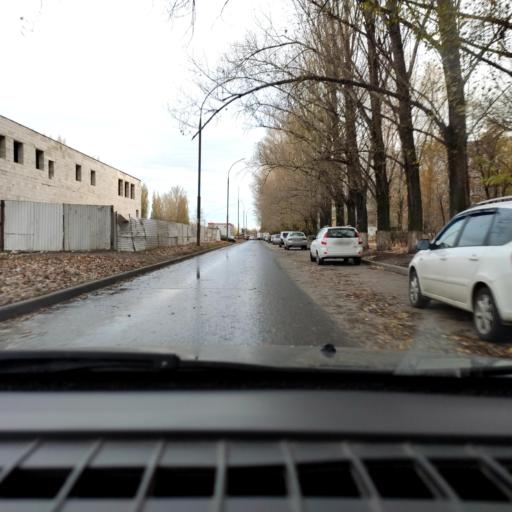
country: RU
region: Samara
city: Tol'yatti
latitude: 53.5250
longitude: 49.2816
